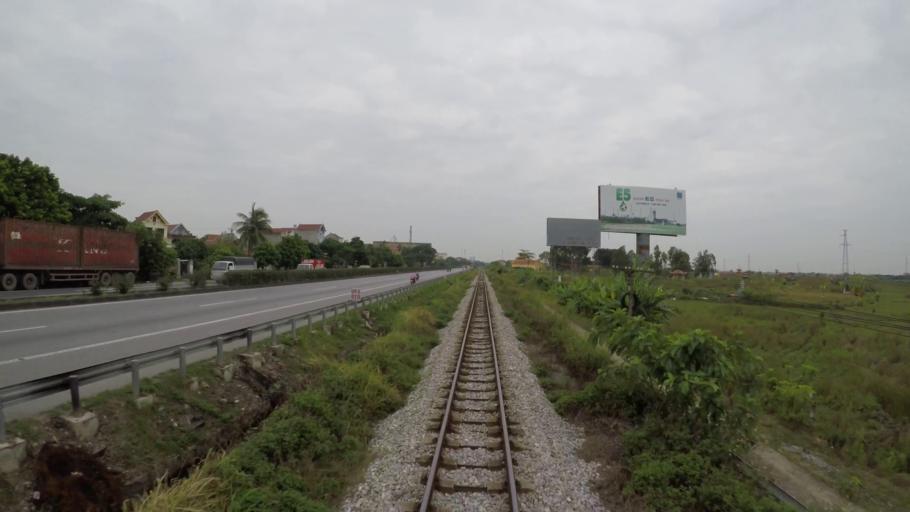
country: VN
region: Hai Duong
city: Phu Thai
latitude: 20.9451
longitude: 106.5417
